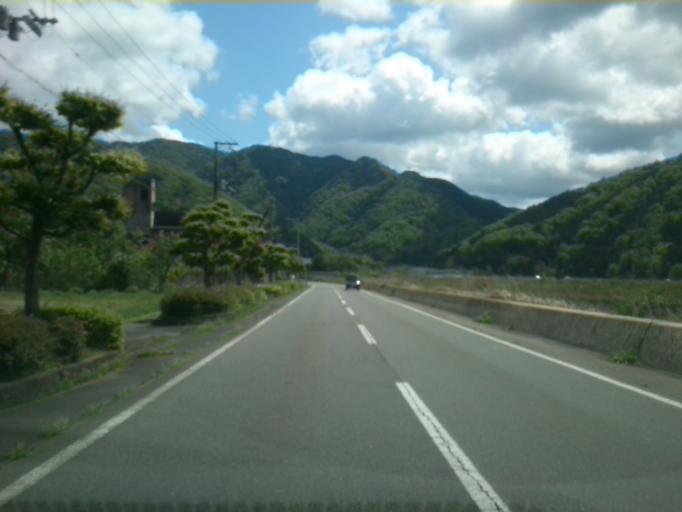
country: JP
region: Hyogo
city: Toyooka
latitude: 35.4523
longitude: 134.8718
